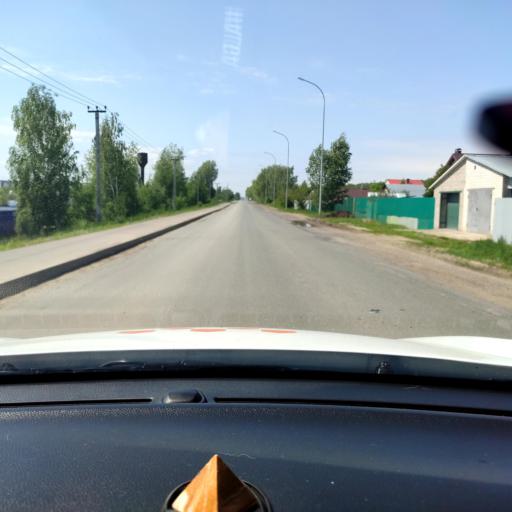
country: RU
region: Tatarstan
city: Stolbishchi
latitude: 55.6976
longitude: 49.1894
